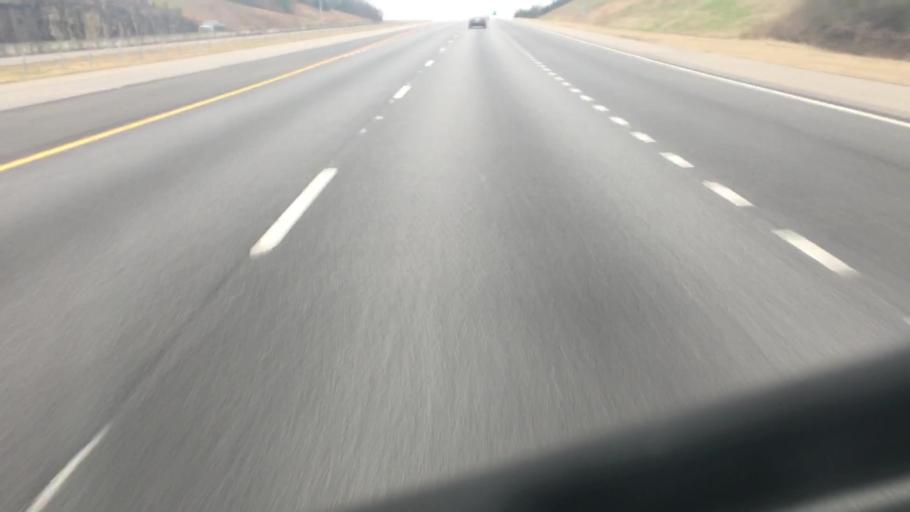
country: US
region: Alabama
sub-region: Jefferson County
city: Fultondale
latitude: 33.5794
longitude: -86.8237
